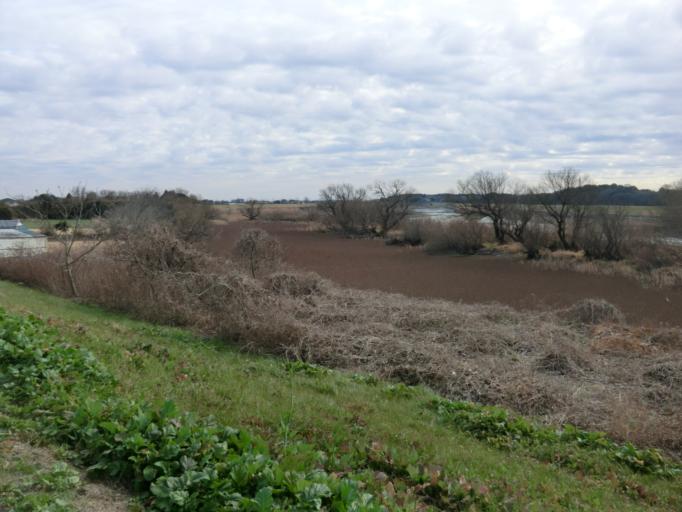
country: JP
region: Ibaraki
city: Moriya
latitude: 35.9387
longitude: 140.0375
